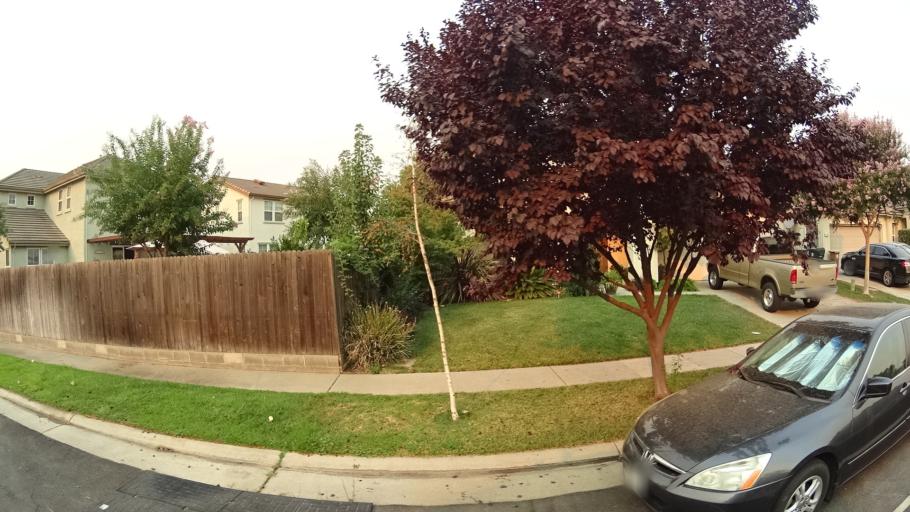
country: US
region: California
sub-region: Sacramento County
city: Laguna
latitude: 38.3810
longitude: -121.4435
